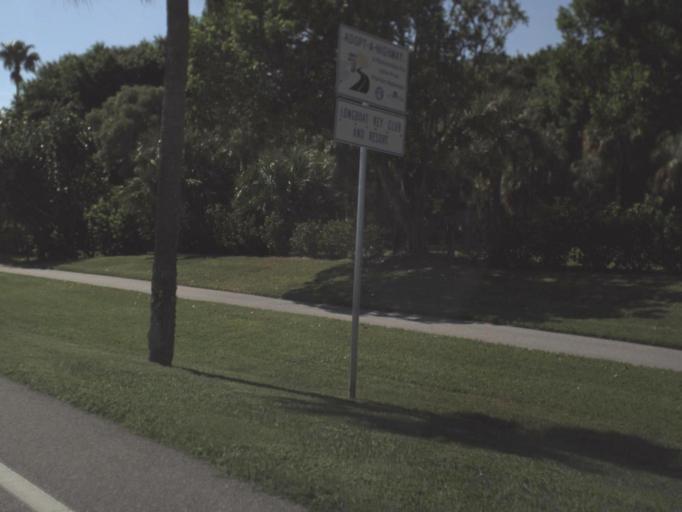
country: US
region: Florida
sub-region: Sarasota County
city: Siesta Key
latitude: 27.3483
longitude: -82.6056
